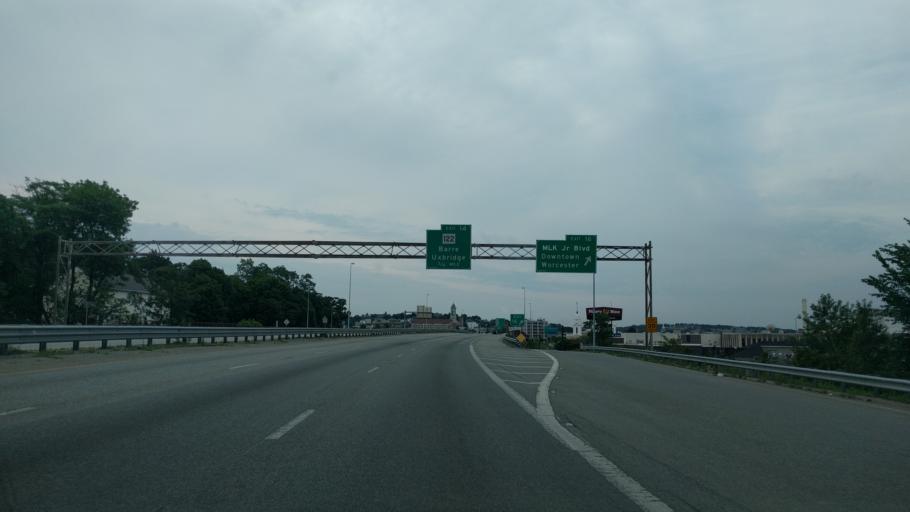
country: US
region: Massachusetts
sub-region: Worcester County
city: Worcester
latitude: 42.2684
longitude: -71.7935
